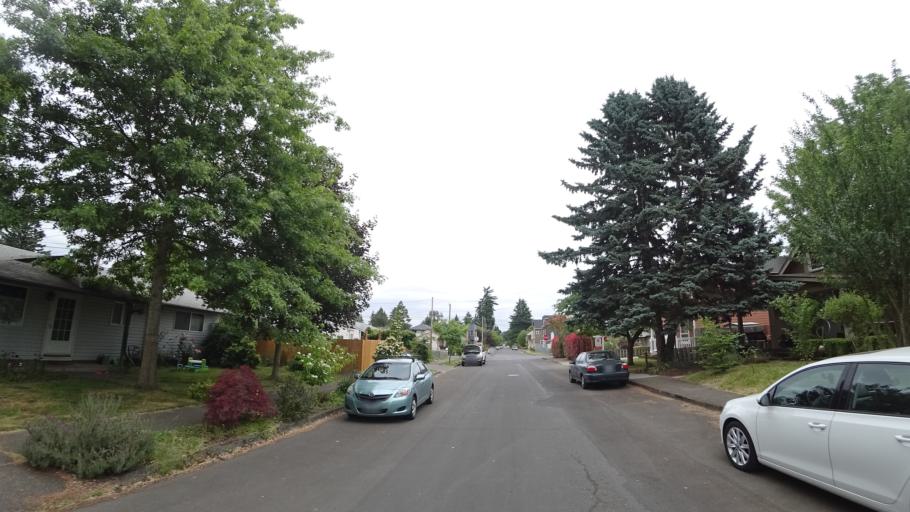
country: US
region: Washington
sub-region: Clark County
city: Vancouver
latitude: 45.5856
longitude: -122.7031
